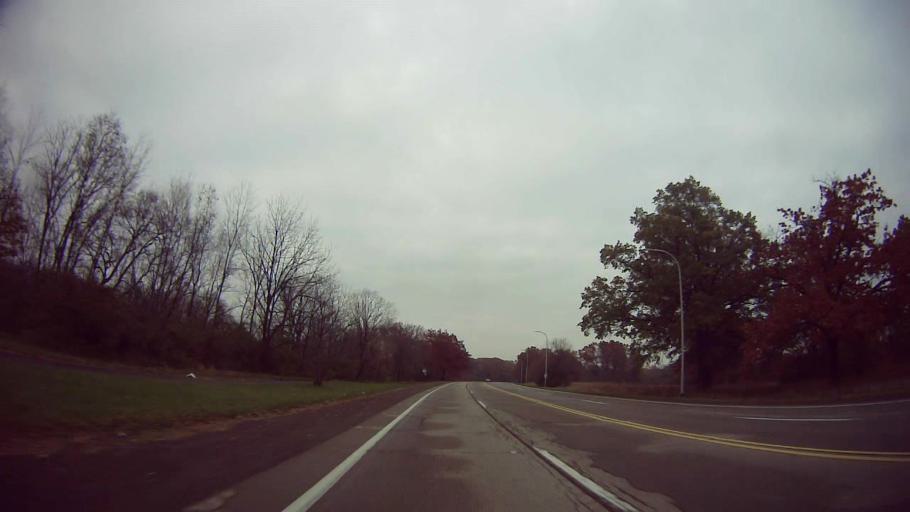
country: US
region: Michigan
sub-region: Wayne County
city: Dearborn Heights
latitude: 42.3551
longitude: -83.2585
